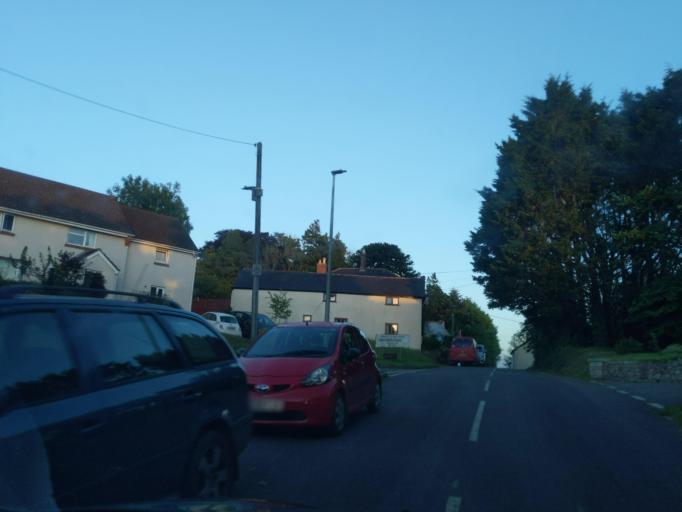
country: GB
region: England
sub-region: Devon
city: Okehampton
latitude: 50.8242
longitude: -4.0718
